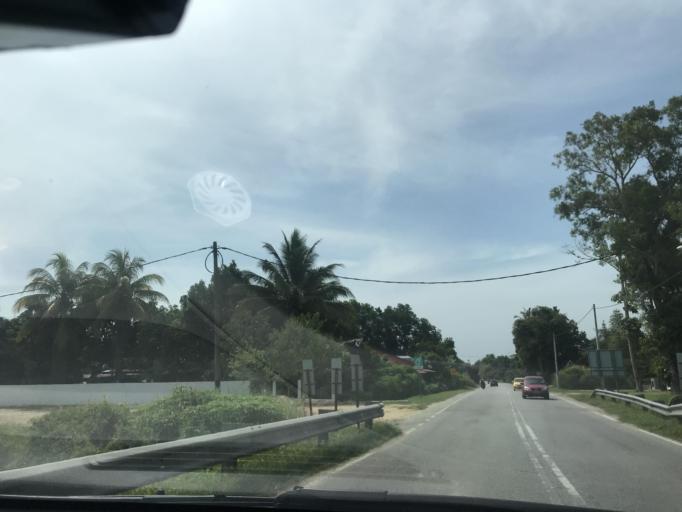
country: MY
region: Kelantan
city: Tumpat
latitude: 6.1874
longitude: 102.1620
